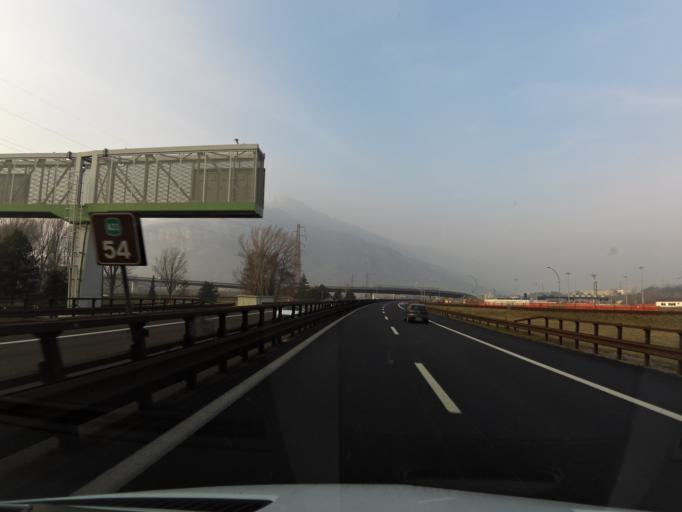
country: IT
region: Trentino-Alto Adige
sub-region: Provincia di Trento
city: Marco
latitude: 45.8442
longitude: 11.0002
